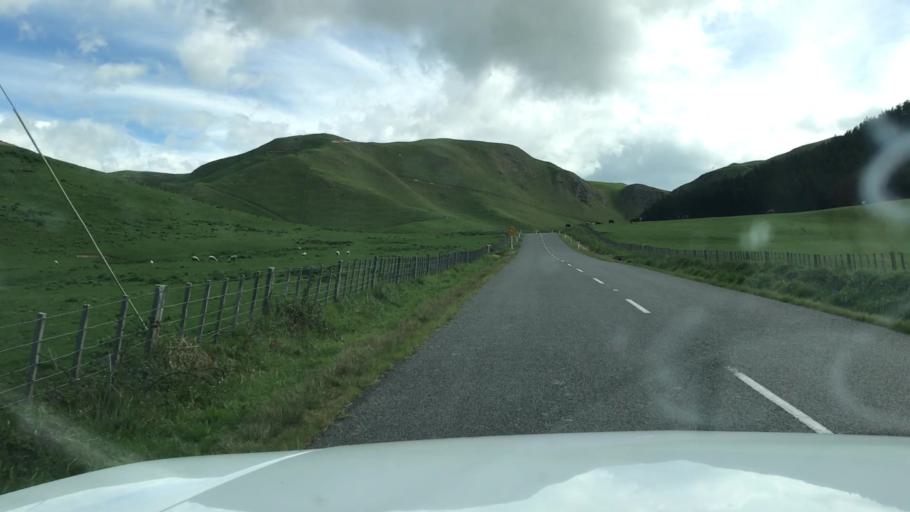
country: NZ
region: Hawke's Bay
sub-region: Hastings District
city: Hastings
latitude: -39.8213
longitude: 176.7356
